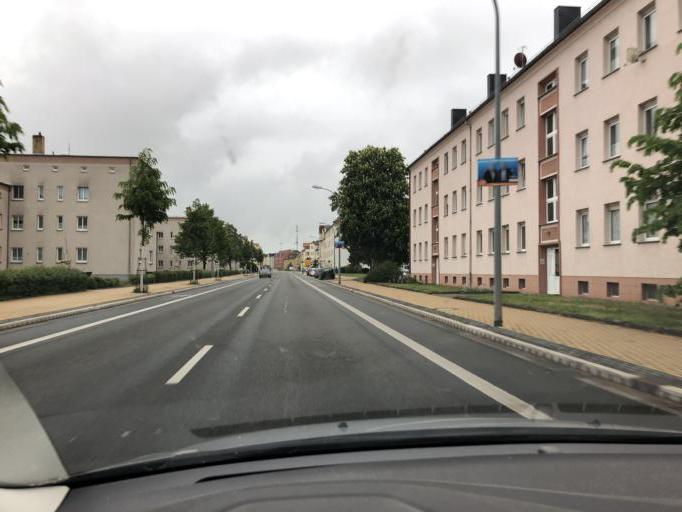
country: DE
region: Saxony
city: Delitzsch
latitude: 51.5332
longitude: 12.3361
